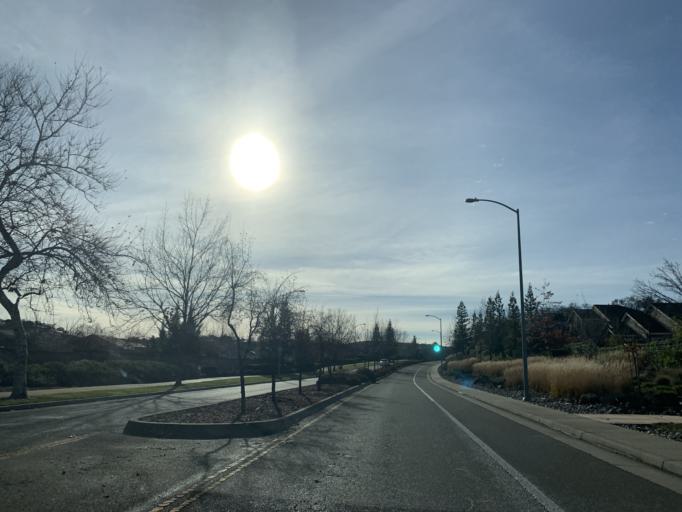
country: US
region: California
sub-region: El Dorado County
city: El Dorado Hills
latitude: 38.6676
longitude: -121.1086
